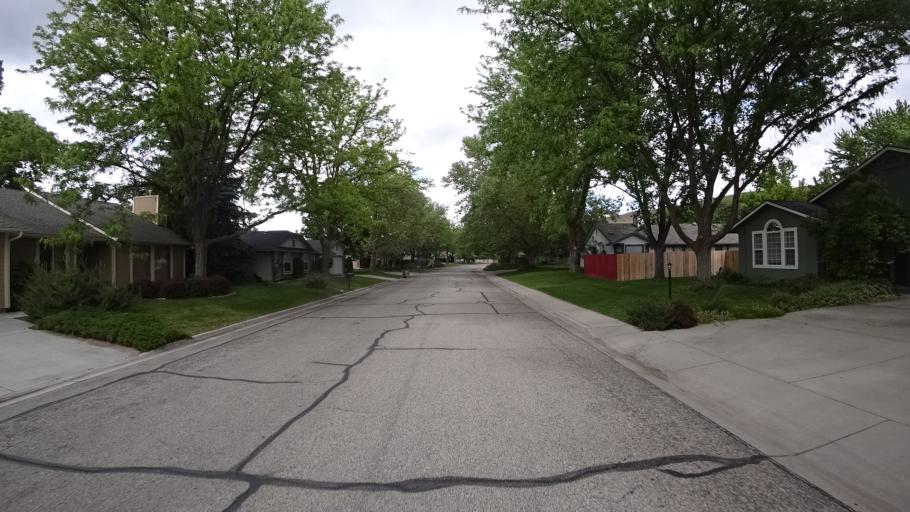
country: US
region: Idaho
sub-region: Ada County
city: Garden City
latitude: 43.6672
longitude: -116.2600
